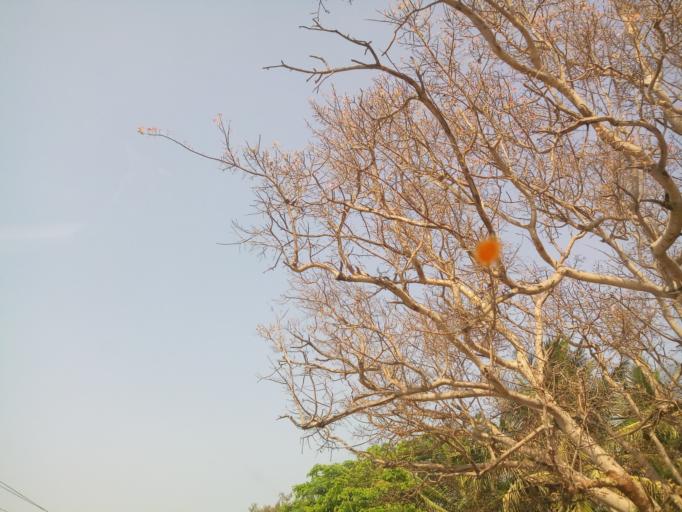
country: IN
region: Karnataka
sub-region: Mandya
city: Shrirangapattana
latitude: 12.3979
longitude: 76.6351
